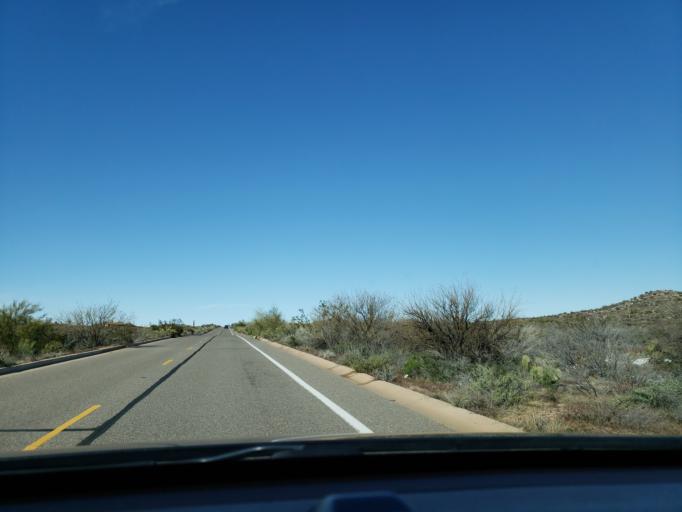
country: US
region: Arizona
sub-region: Maricopa County
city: Carefree
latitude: 33.7181
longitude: -111.8264
